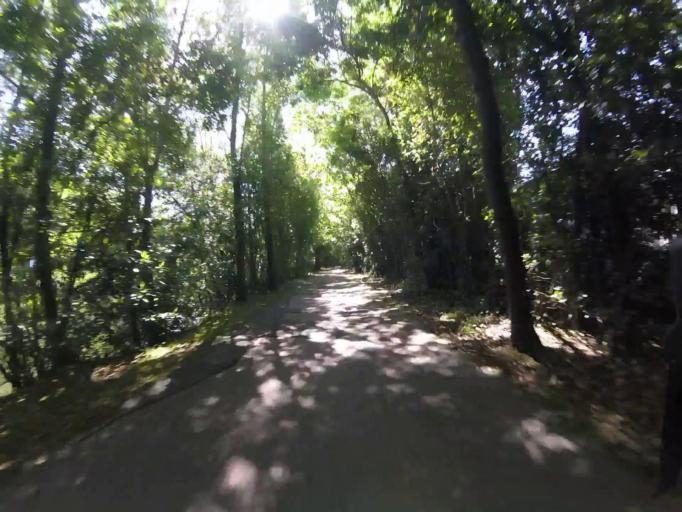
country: ES
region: Basque Country
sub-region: Provincia de Guipuzcoa
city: Irun
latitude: 43.3421
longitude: -1.7550
